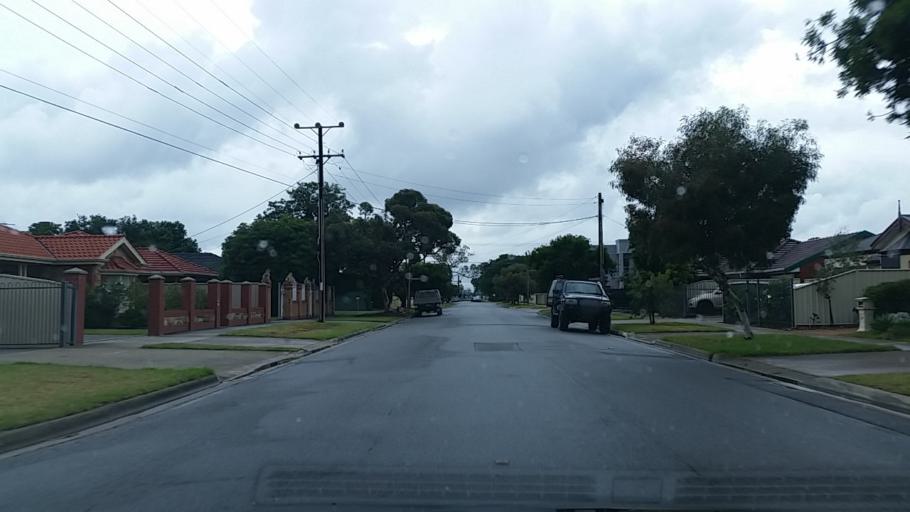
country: AU
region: South Australia
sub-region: Charles Sturt
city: Seaton
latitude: -34.8959
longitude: 138.5167
